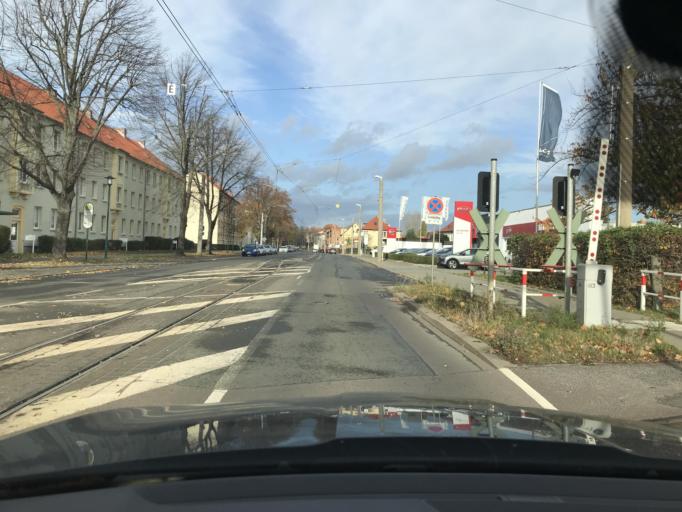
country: DE
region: Saxony-Anhalt
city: Halberstadt
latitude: 51.8836
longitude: 11.0564
